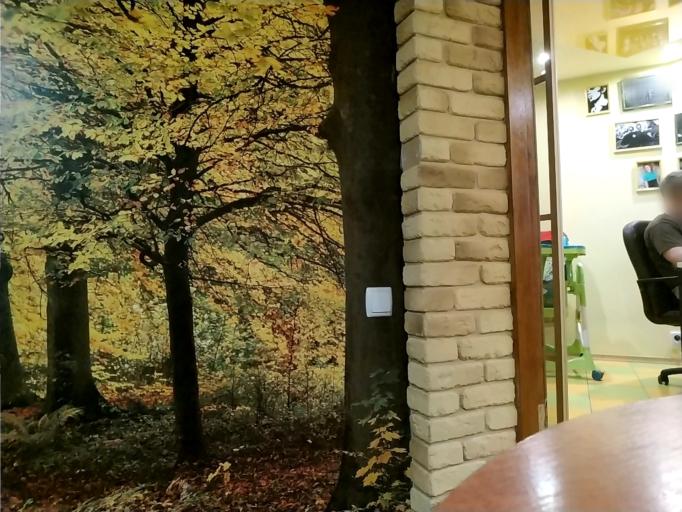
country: RU
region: Tverskaya
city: Zapadnaya Dvina
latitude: 56.3302
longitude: 31.8906
